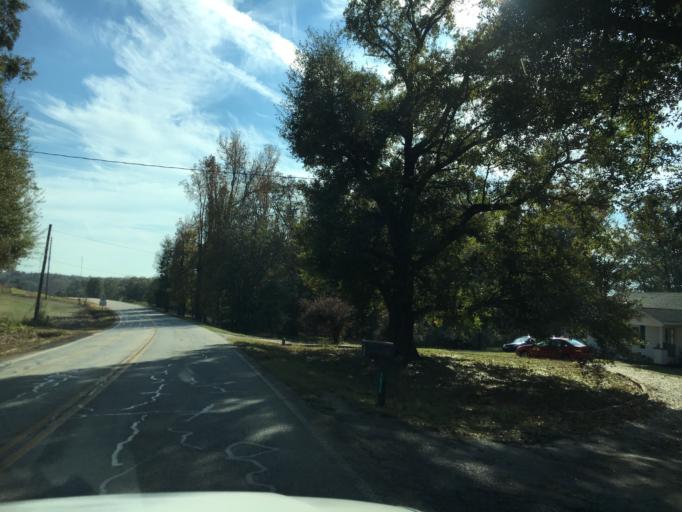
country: US
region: Georgia
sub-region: Hart County
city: Hartwell
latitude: 34.2531
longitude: -82.9011
